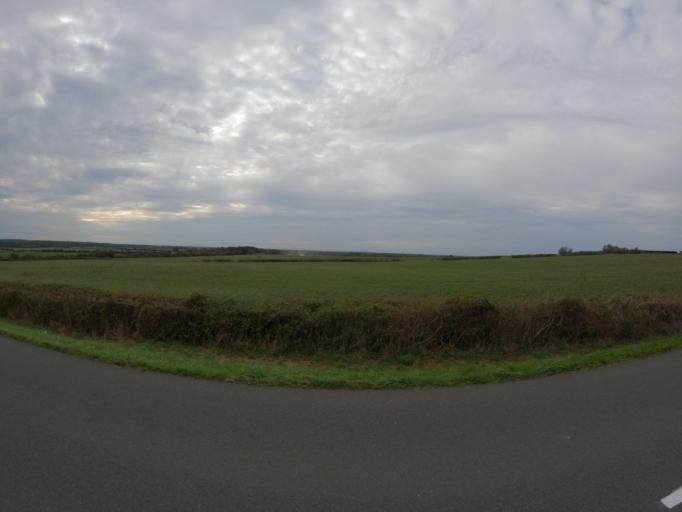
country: FR
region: Poitou-Charentes
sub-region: Departement de la Vienne
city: Saulge
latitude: 46.3815
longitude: 0.8474
